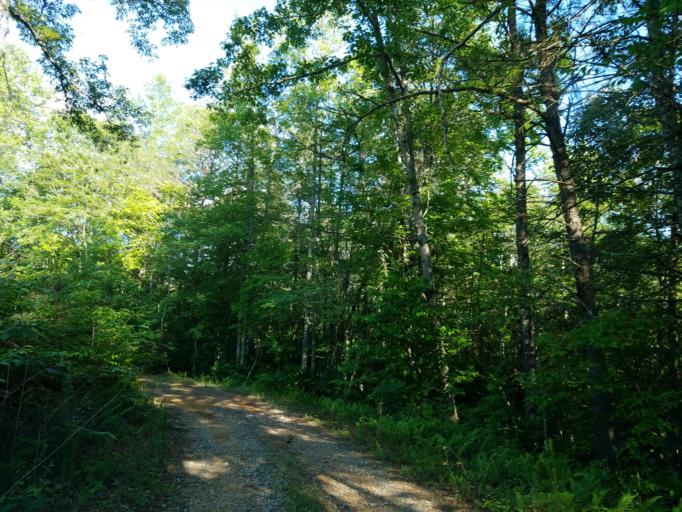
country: US
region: Georgia
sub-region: Fannin County
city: Blue Ridge
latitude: 34.7966
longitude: -84.1958
